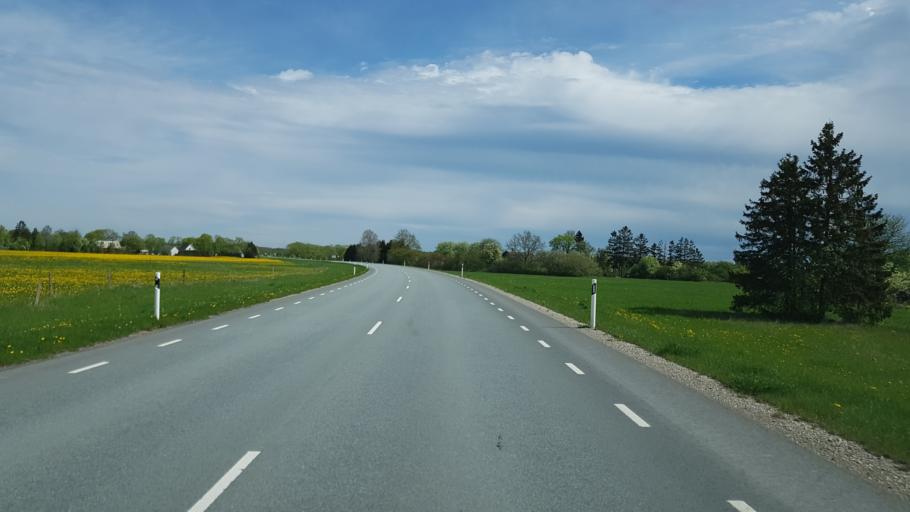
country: EE
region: Saare
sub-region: Kuressaare linn
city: Kuressaare
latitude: 58.2957
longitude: 22.5712
